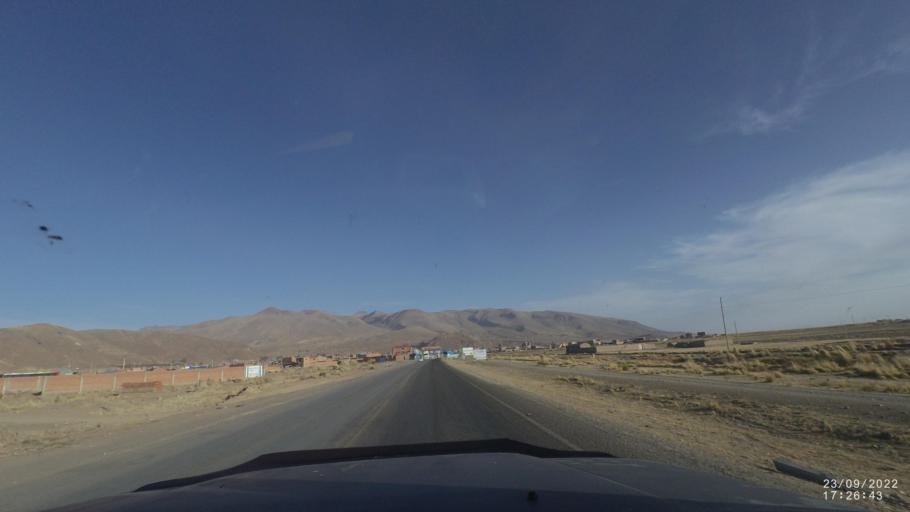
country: BO
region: Oruro
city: Challapata
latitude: -18.8883
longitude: -66.7830
